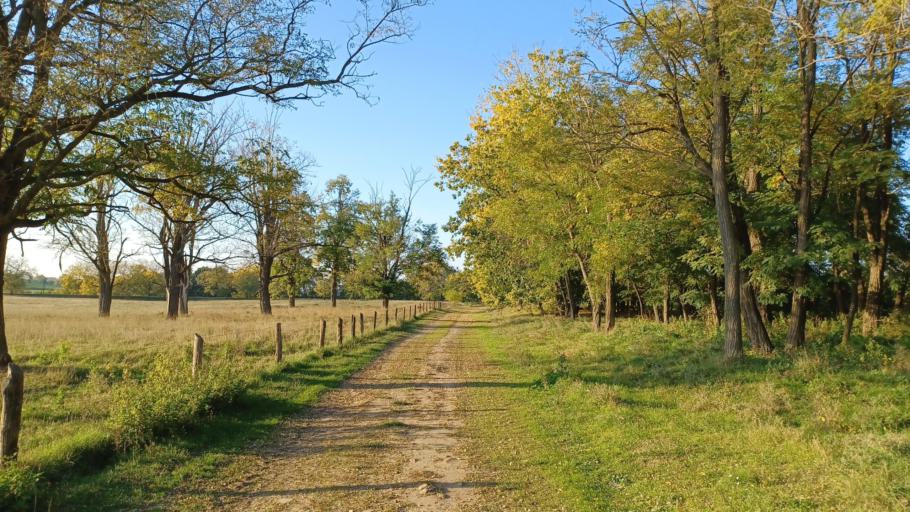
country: HU
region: Tolna
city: Tengelic
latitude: 46.5431
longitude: 18.6861
